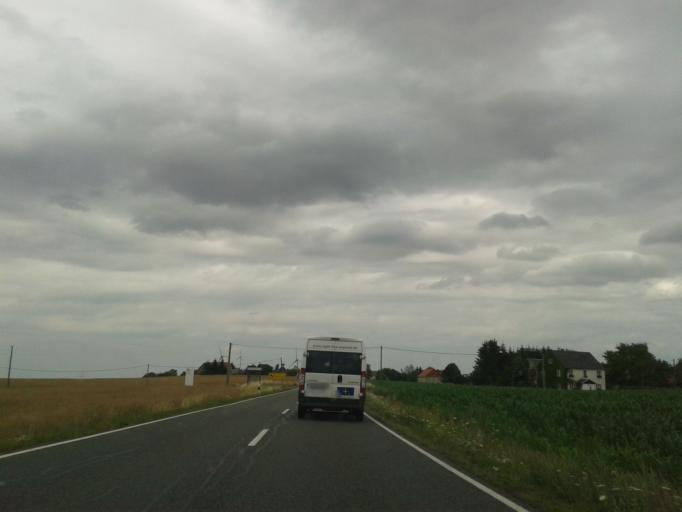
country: DE
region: Saxony
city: Niederschona
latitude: 50.9747
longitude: 13.4392
